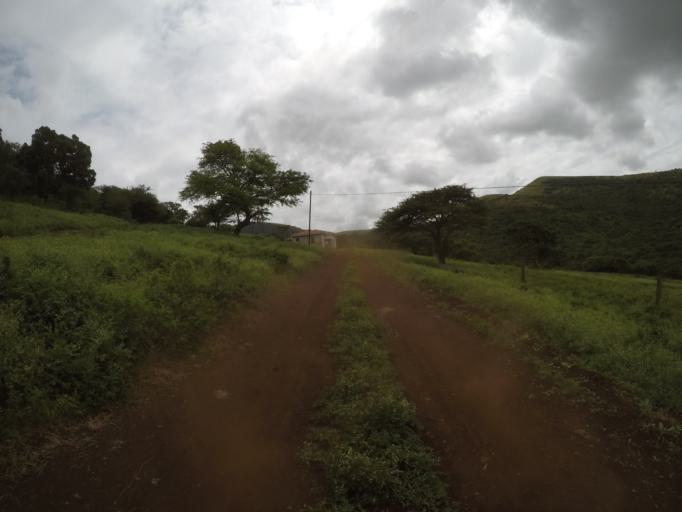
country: ZA
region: KwaZulu-Natal
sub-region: uThungulu District Municipality
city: Empangeni
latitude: -28.5804
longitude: 31.8890
